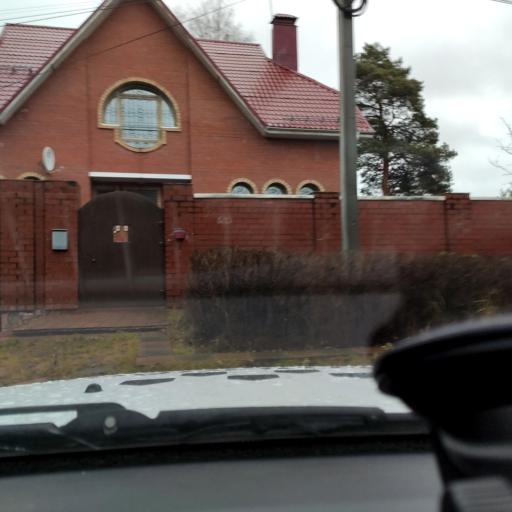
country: RU
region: Perm
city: Perm
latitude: 58.0606
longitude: 56.3059
